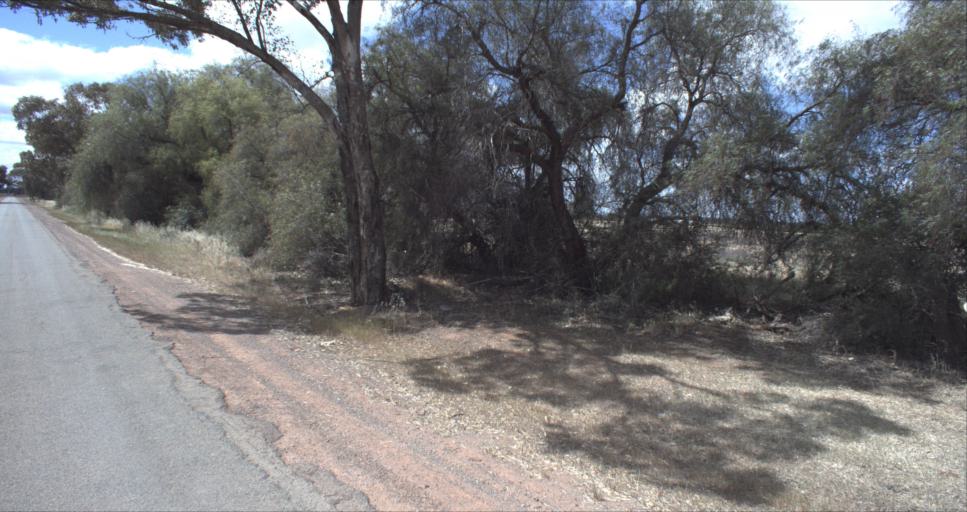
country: AU
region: New South Wales
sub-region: Leeton
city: Leeton
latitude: -34.5884
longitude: 146.3956
